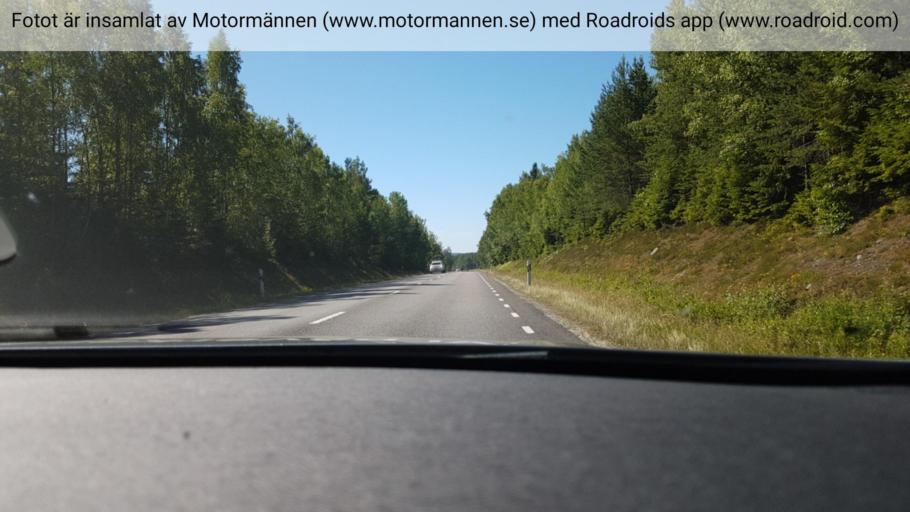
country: SE
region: Joenkoeping
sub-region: Habo Kommun
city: Habo
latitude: 57.9750
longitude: 14.1052
